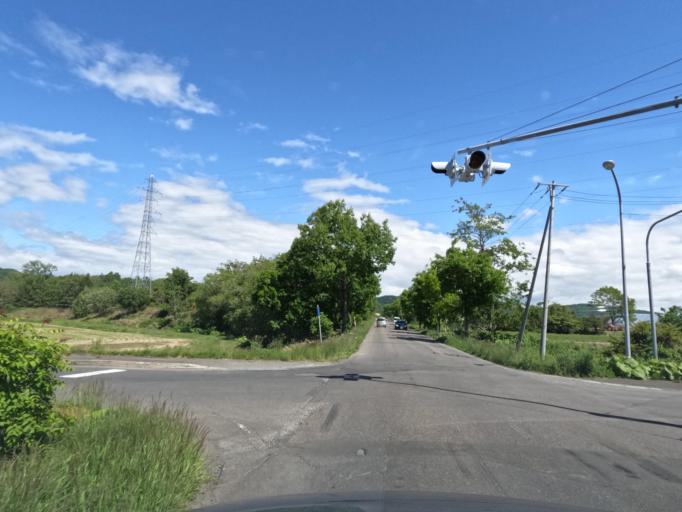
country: JP
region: Hokkaido
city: Kitahiroshima
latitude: 43.0194
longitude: 141.7142
